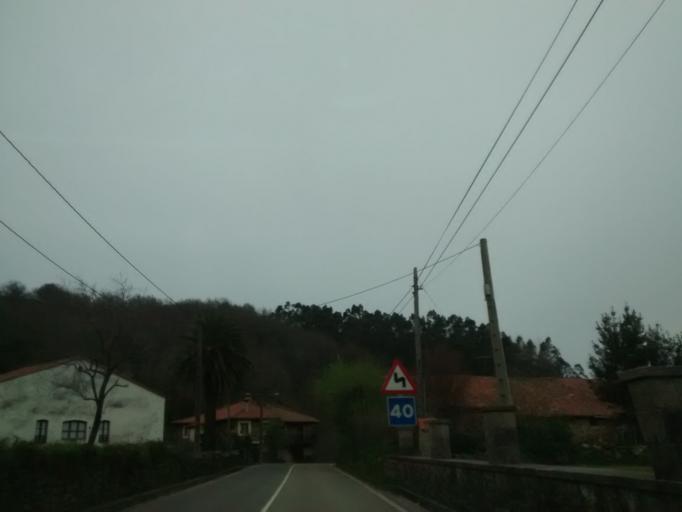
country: ES
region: Cantabria
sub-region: Provincia de Cantabria
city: Lierganes
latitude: 43.3493
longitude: -3.7299
